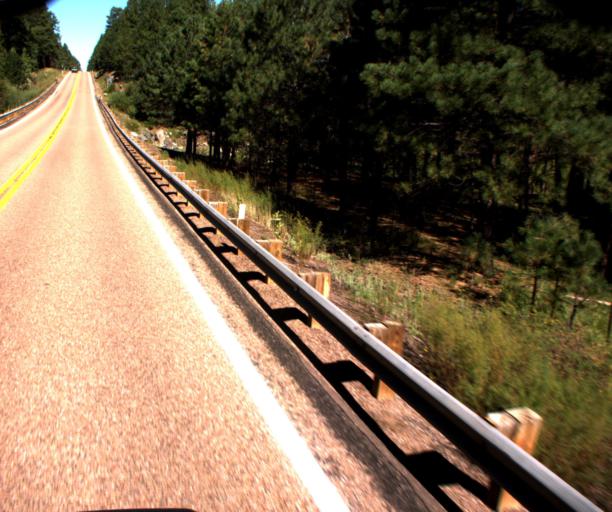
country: US
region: Arizona
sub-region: Navajo County
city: Pinetop-Lakeside
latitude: 34.0535
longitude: -109.7534
